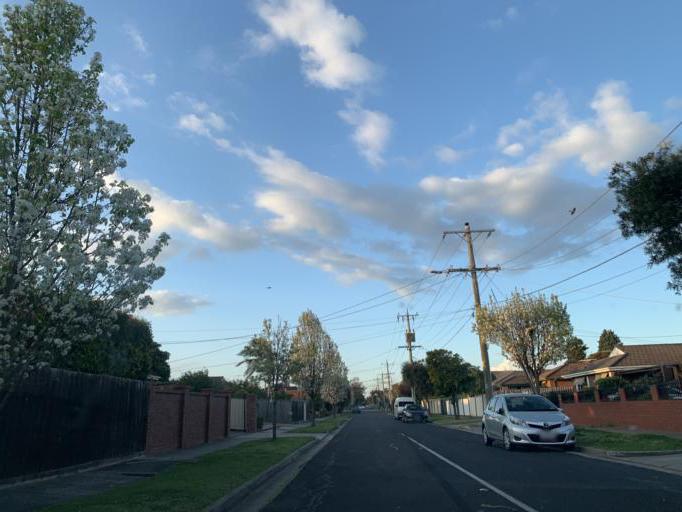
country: AU
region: Victoria
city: Heatherton
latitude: -37.9706
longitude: 145.0823
